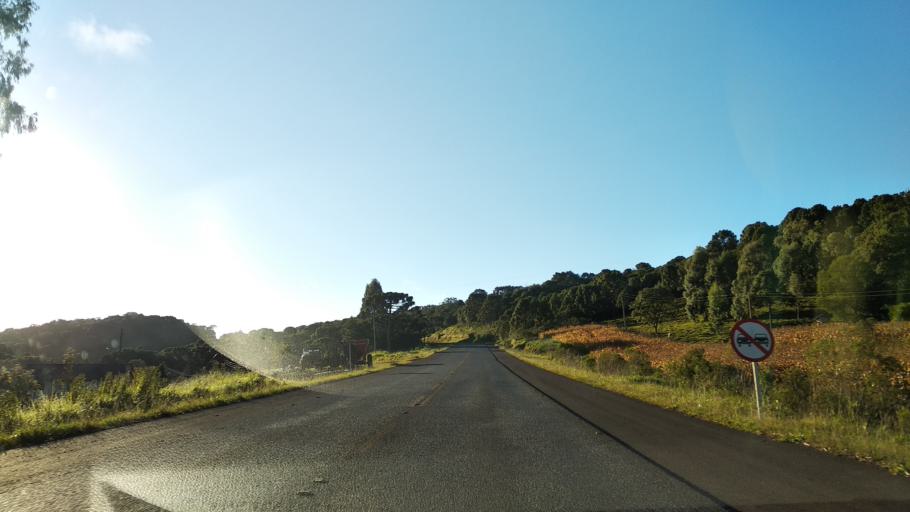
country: BR
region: Santa Catarina
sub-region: Correia Pinto
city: Correia Pinto
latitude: -27.6162
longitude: -50.6852
